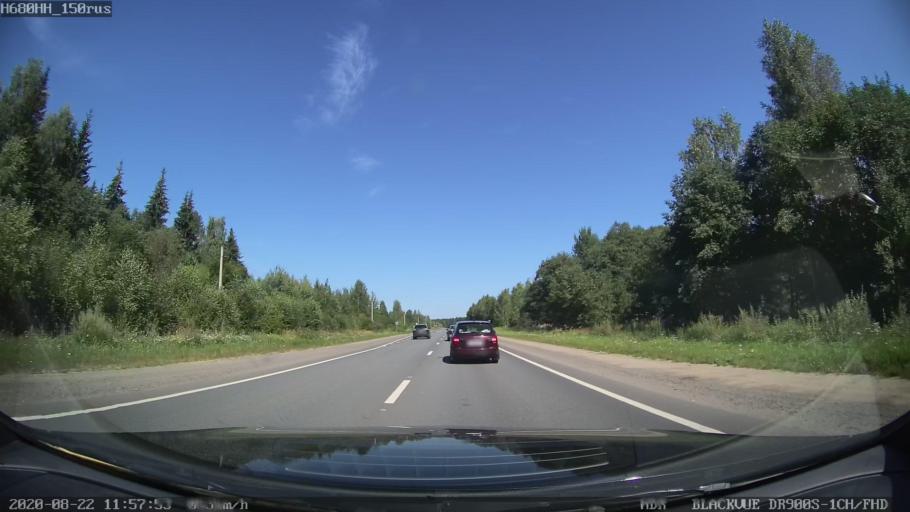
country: RU
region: Tverskaya
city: Rameshki
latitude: 57.1852
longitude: 36.0823
